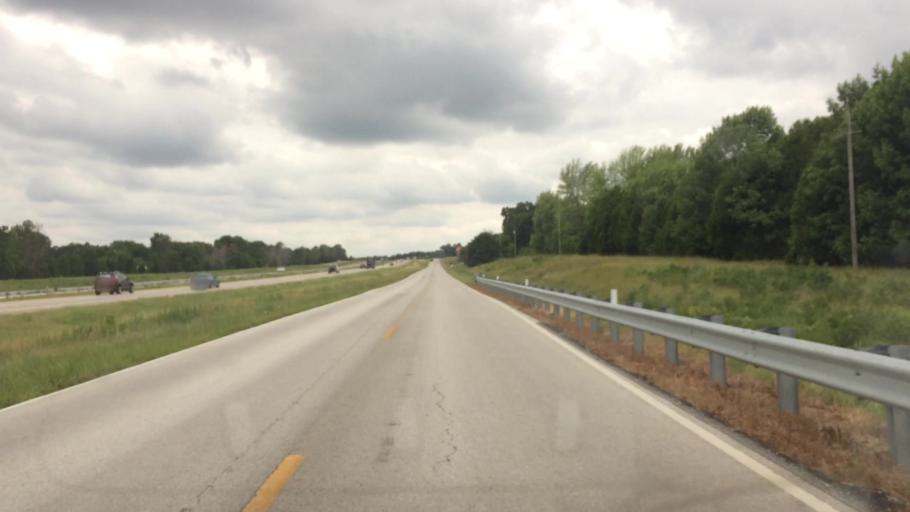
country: US
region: Missouri
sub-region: Greene County
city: Strafford
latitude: 37.2888
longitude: -93.0331
